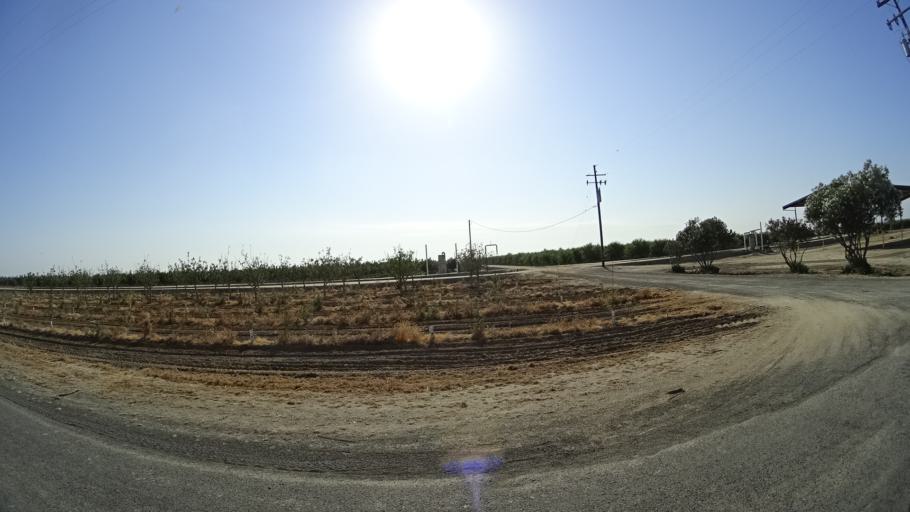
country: US
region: California
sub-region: Kings County
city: Home Garden
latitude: 36.2770
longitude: -119.5652
